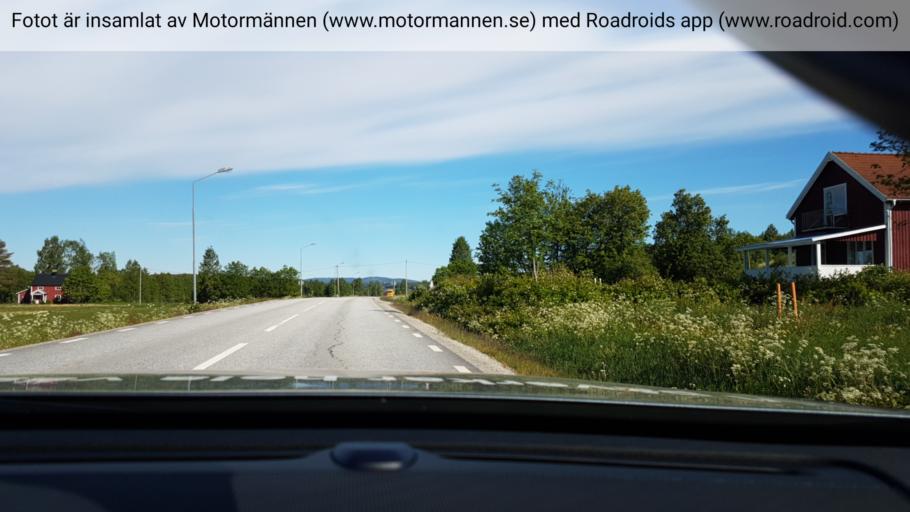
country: SE
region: Vaesterbotten
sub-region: Vindelns Kommun
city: Vindeln
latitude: 64.1668
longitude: 19.4958
